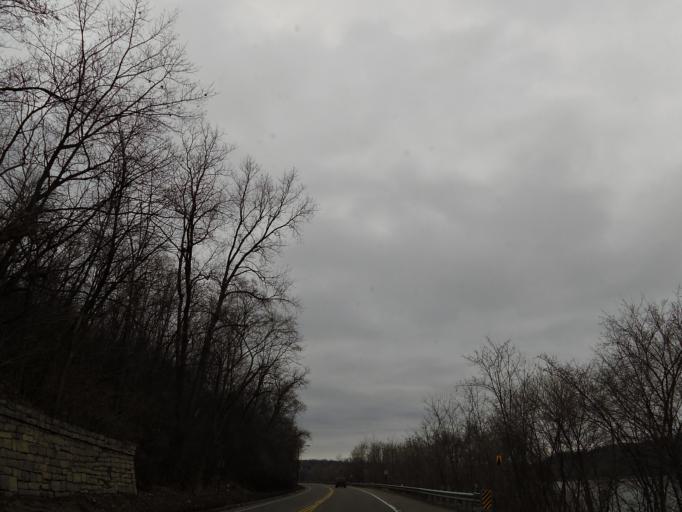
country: US
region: Minnesota
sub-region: Washington County
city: Stillwater
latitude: 45.0459
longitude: -92.7968
